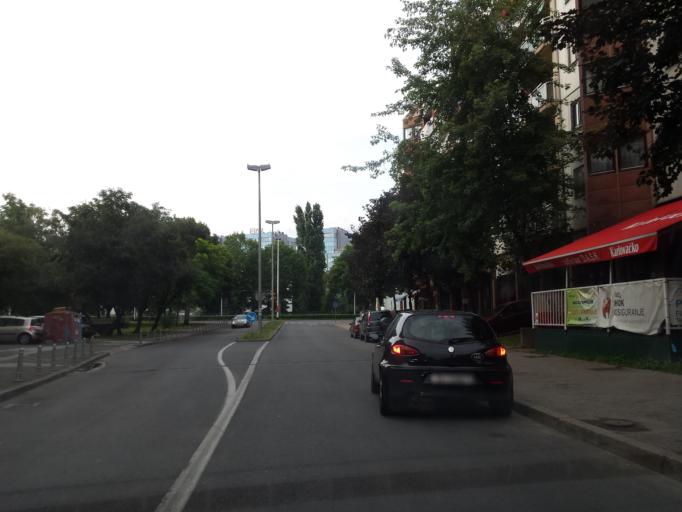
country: HR
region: Grad Zagreb
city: Novi Zagreb
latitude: 45.8004
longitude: 16.0009
